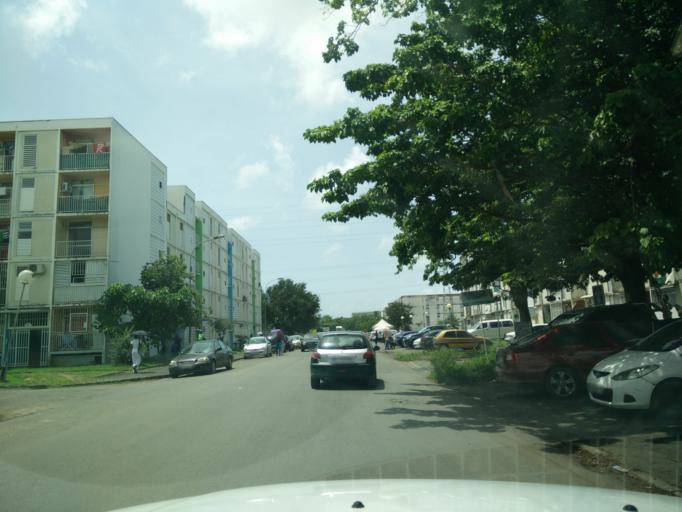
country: GP
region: Guadeloupe
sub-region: Guadeloupe
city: Pointe-a-Pitre
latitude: 16.2556
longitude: -61.5301
